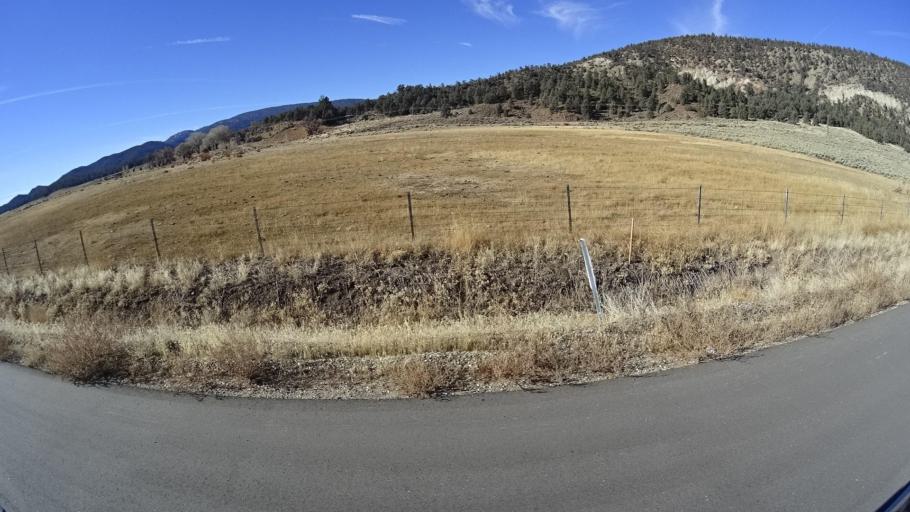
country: US
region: California
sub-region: Kern County
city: Frazier Park
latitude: 34.8103
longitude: -119.0118
